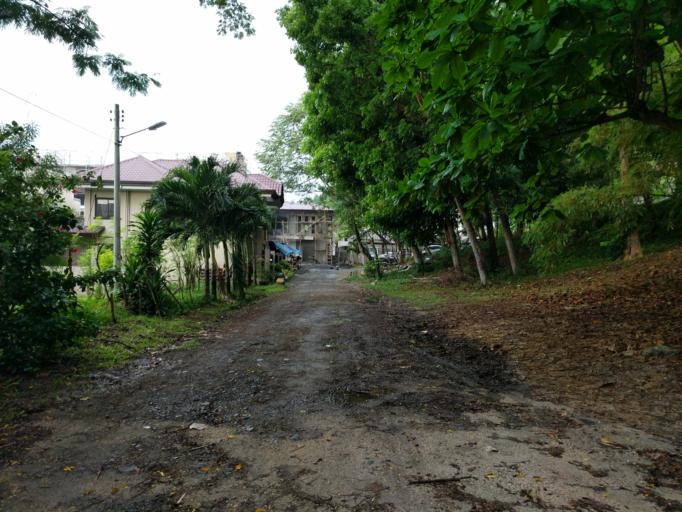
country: PH
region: Davao
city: Davao
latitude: 7.0781
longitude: 125.5820
